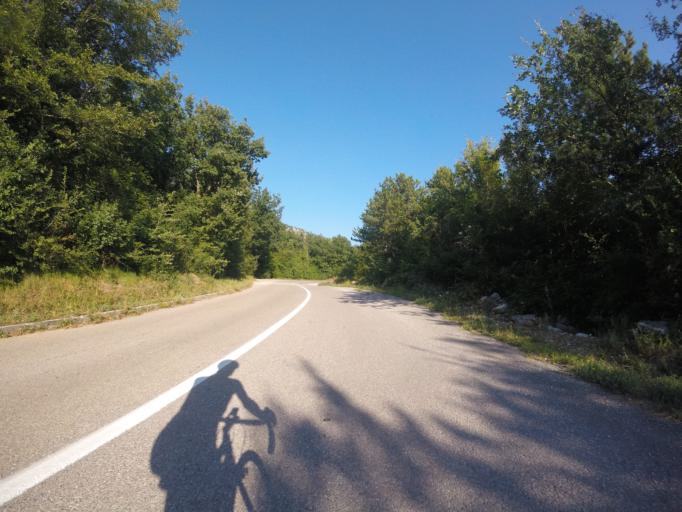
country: HR
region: Primorsko-Goranska
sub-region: Grad Crikvenica
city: Crikvenica
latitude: 45.2164
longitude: 14.6957
